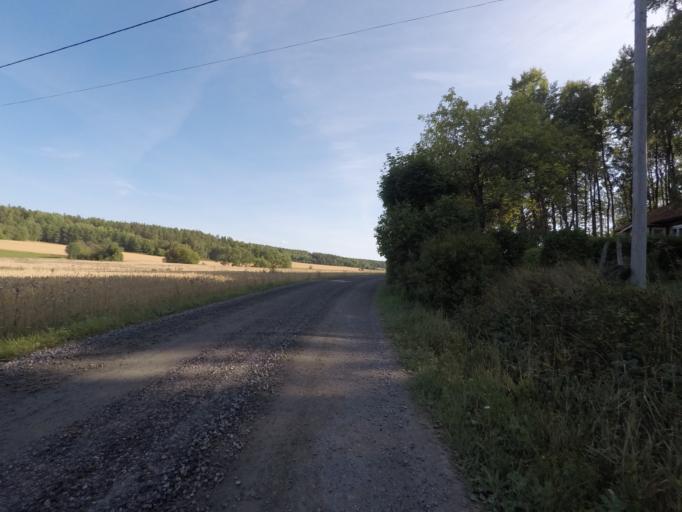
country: SE
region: Soedermanland
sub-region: Eskilstuna Kommun
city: Kvicksund
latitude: 59.4191
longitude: 16.2644
